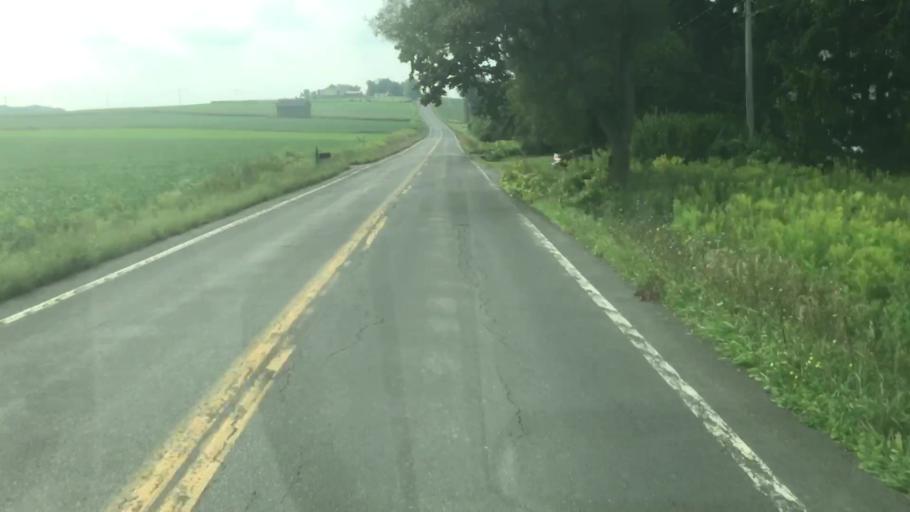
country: US
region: New York
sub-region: Onondaga County
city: Skaneateles
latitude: 42.8976
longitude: -76.4529
